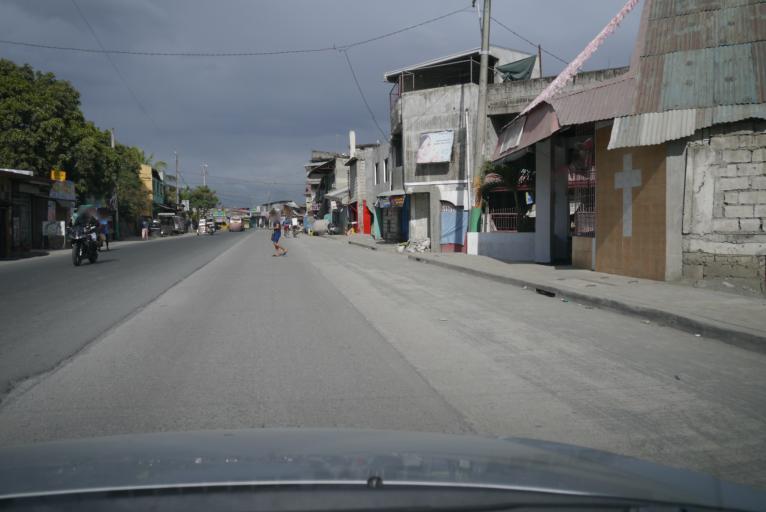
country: PH
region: Calabarzon
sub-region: Province of Rizal
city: Taytay
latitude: 14.5439
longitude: 121.1254
